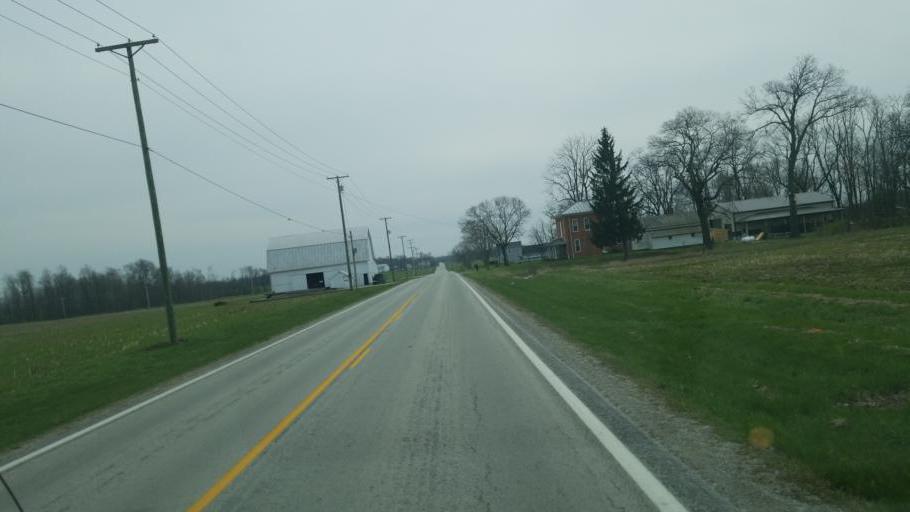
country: US
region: Ohio
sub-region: Wyandot County
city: Carey
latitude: 41.0087
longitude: -83.2802
